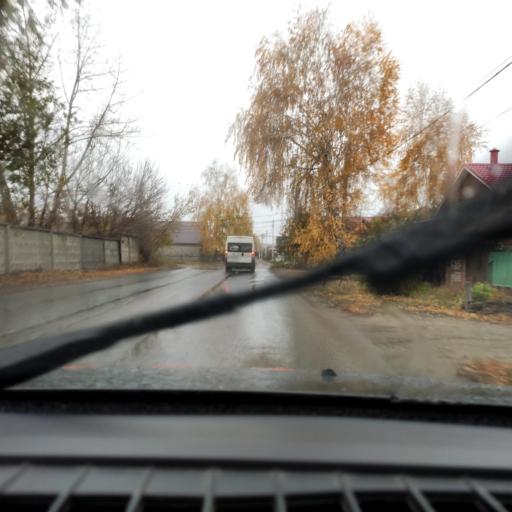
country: RU
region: Samara
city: Tol'yatti
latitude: 53.5377
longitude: 49.4256
